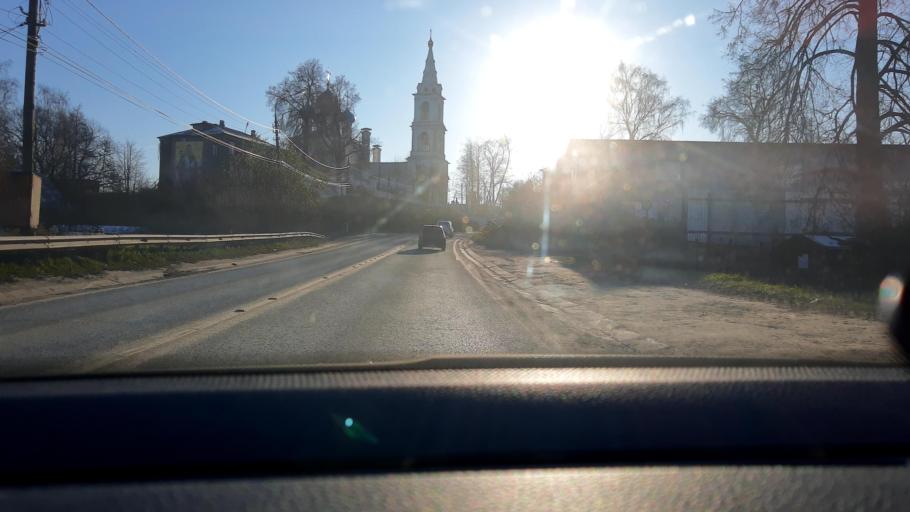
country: RU
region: Moskovskaya
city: Lesnyye Polyany
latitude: 55.9902
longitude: 37.8677
